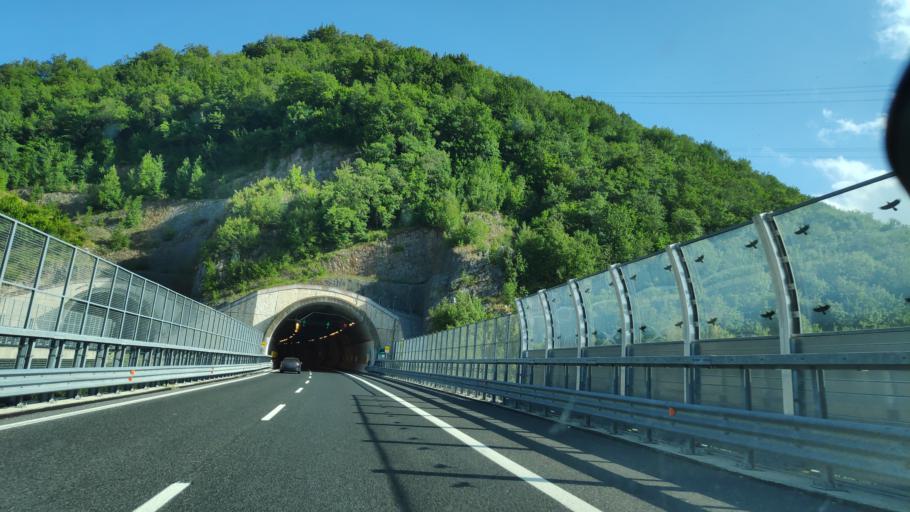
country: IT
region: Campania
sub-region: Provincia di Salerno
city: Casalbuono
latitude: 40.2142
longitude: 15.6727
